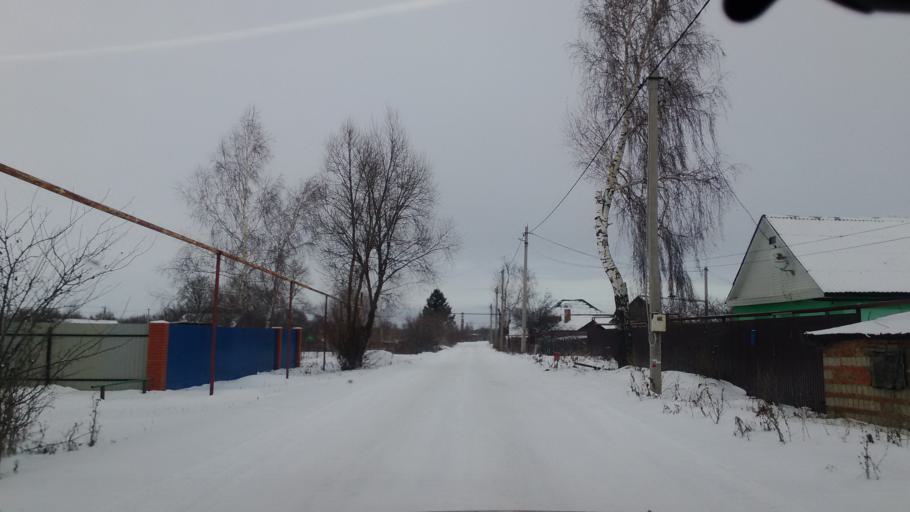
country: RU
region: Tula
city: Bogoroditsk
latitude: 53.7539
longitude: 38.1061
